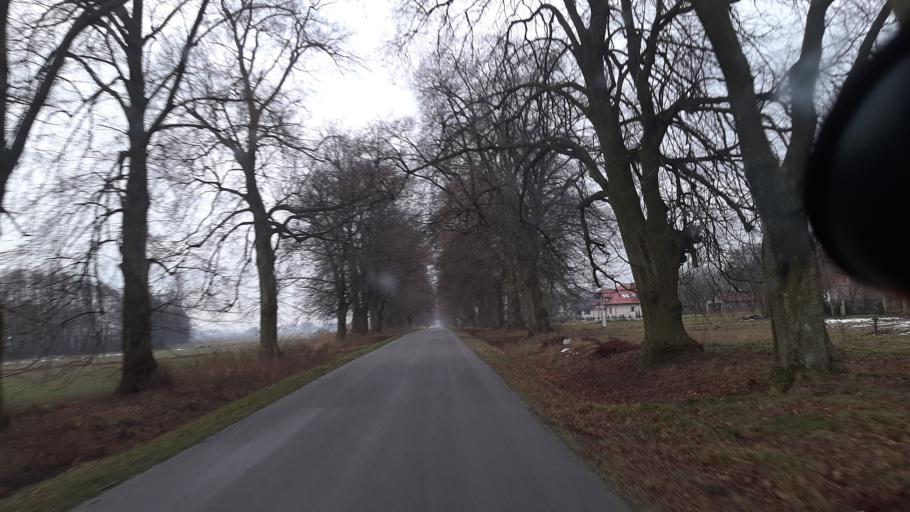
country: PL
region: Lublin Voivodeship
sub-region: Powiat lubelski
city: Jastkow
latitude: 51.3455
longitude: 22.5242
